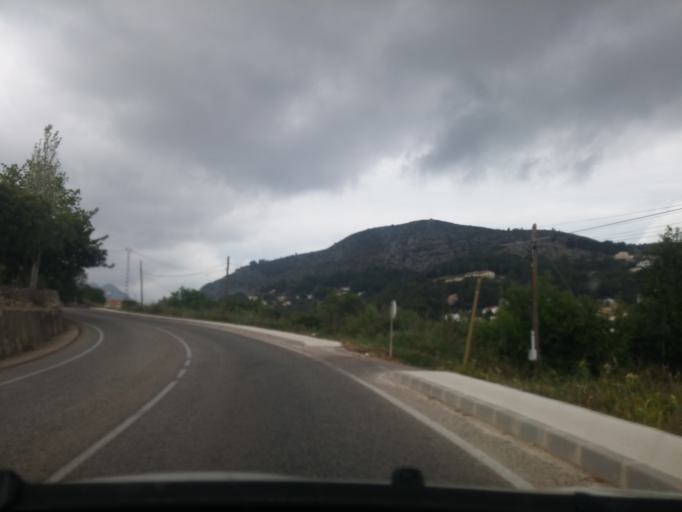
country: ES
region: Valencia
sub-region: Provincia de Alicante
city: Alcalali
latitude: 38.7510
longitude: -0.0390
